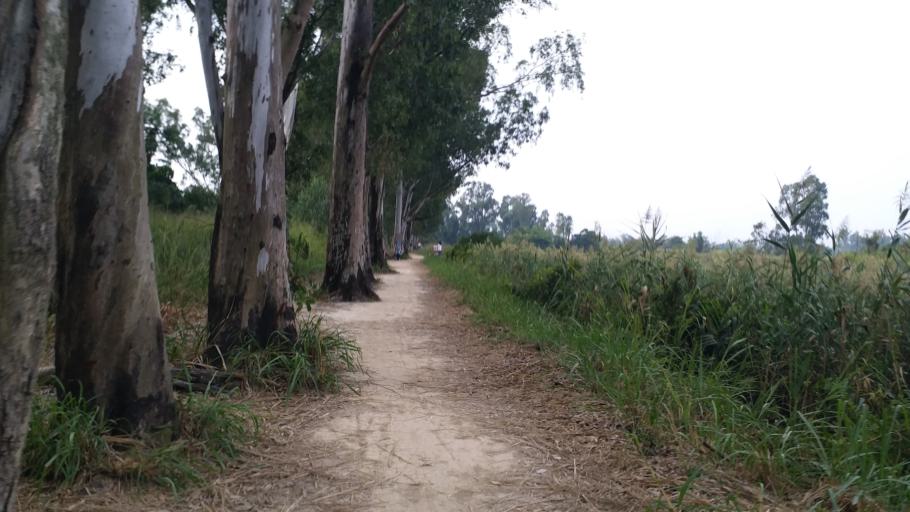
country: HK
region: Yuen Long
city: Yuen Long Kau Hui
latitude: 22.4566
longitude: 114.0345
